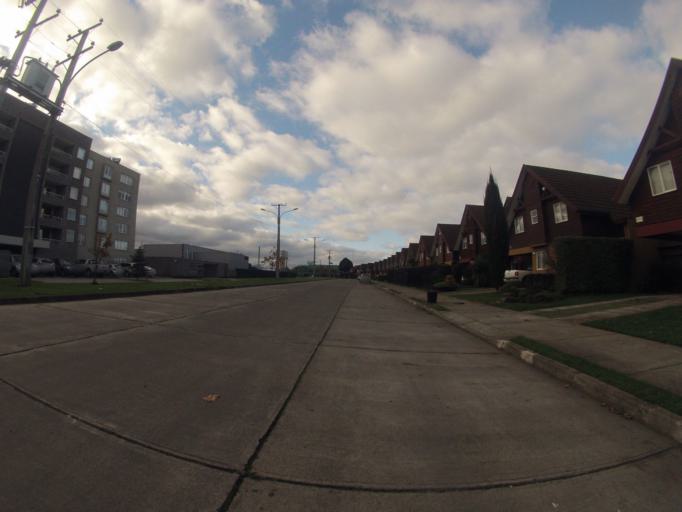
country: CL
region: Araucania
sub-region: Provincia de Cautin
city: Temuco
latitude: -38.7420
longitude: -72.6431
